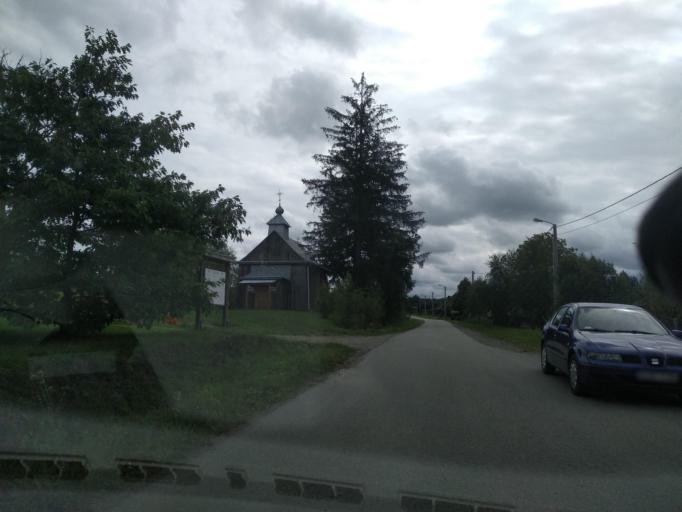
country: PL
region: Lesser Poland Voivodeship
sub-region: Powiat gorlicki
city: Uscie Gorlickie
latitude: 49.5456
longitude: 21.1901
